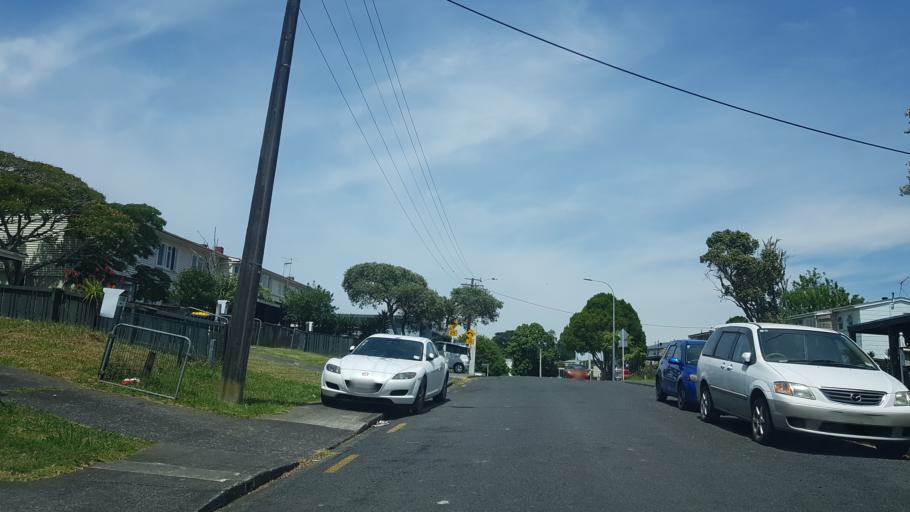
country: NZ
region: Auckland
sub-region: Auckland
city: North Shore
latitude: -36.7990
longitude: 174.7487
